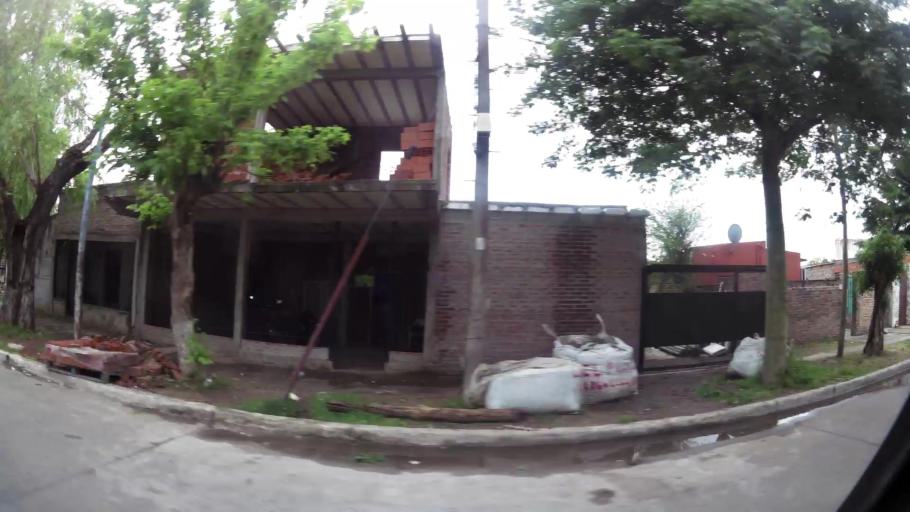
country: AR
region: Buenos Aires
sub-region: Partido de Lanus
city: Lanus
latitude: -34.7284
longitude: -58.3459
